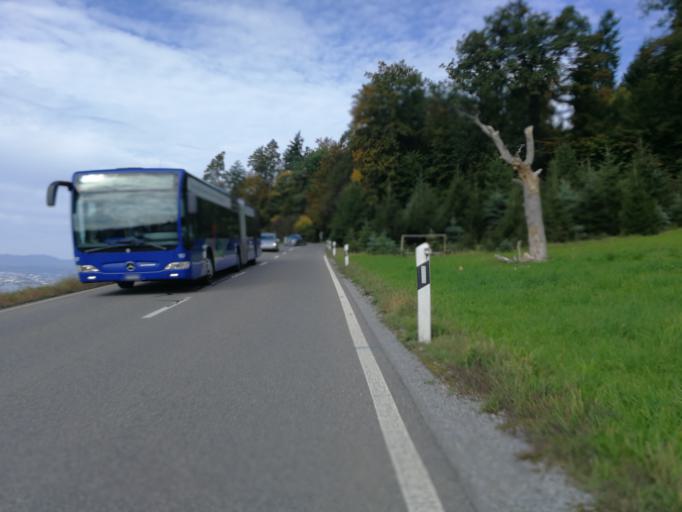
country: CH
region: Zurich
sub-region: Bezirk Meilen
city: Oetwil am See
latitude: 47.2626
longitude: 8.7108
